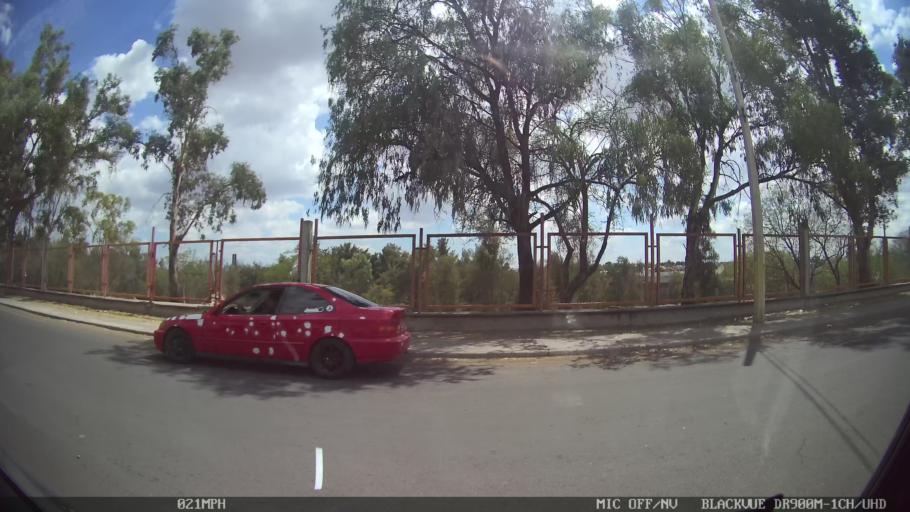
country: MX
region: Jalisco
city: Tlaquepaque
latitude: 20.6757
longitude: -103.2649
